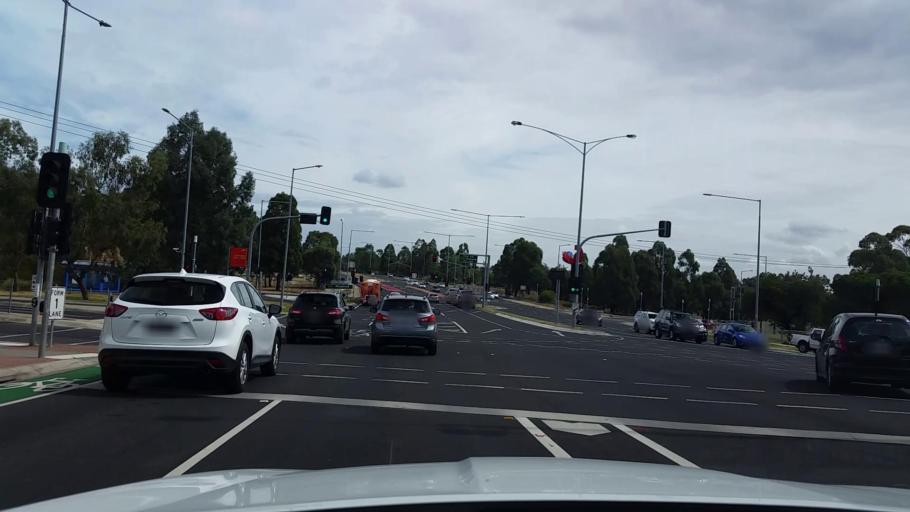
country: AU
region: Victoria
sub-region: Boroondara
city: Balwyn North
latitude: -37.7883
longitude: 145.1051
